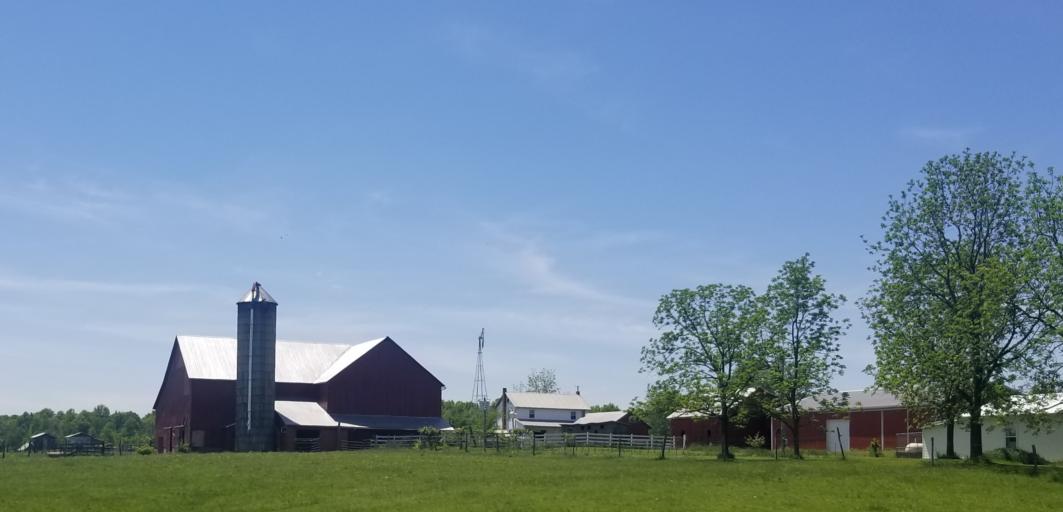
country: US
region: Ohio
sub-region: Wayne County
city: West Salem
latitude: 40.9740
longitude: -82.1803
